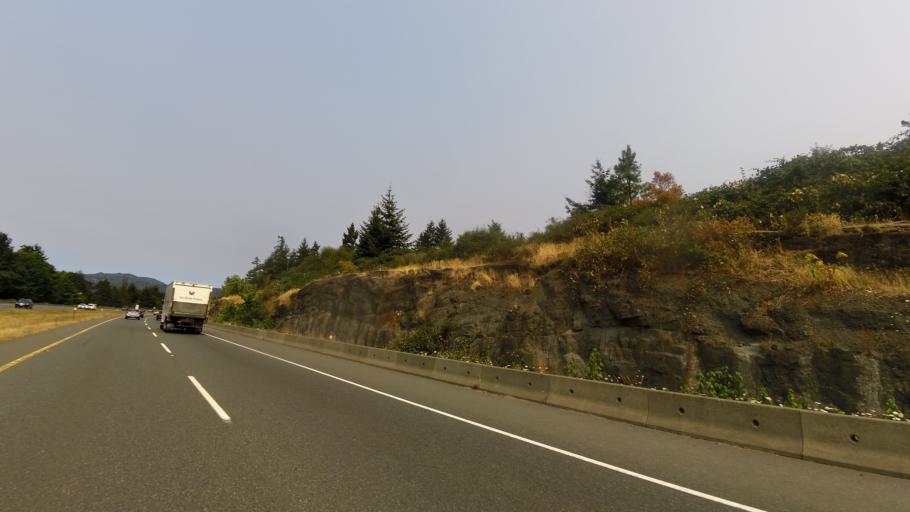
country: CA
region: British Columbia
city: Nanaimo
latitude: 49.1947
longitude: -124.0202
